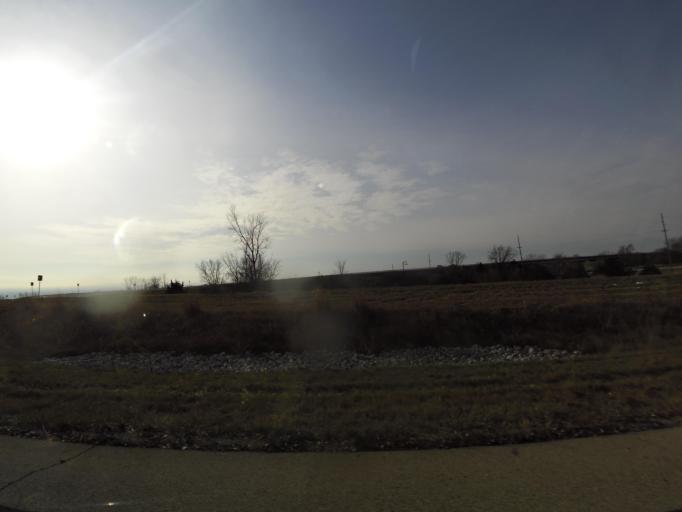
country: US
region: Illinois
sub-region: Macon County
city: Decatur
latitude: 39.7865
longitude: -88.9750
